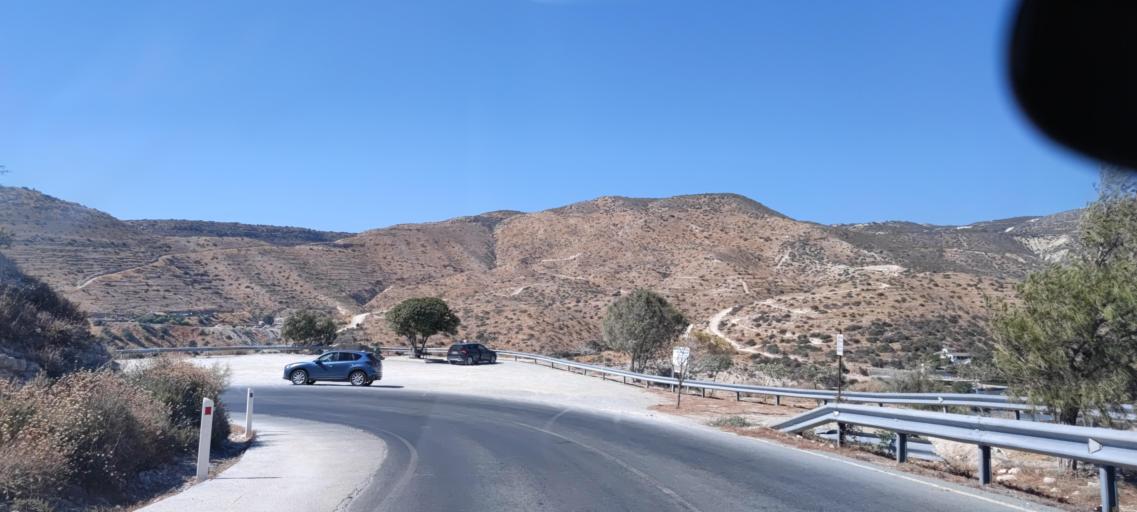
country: CY
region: Limassol
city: Mouttagiaka
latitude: 34.7438
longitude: 33.0875
